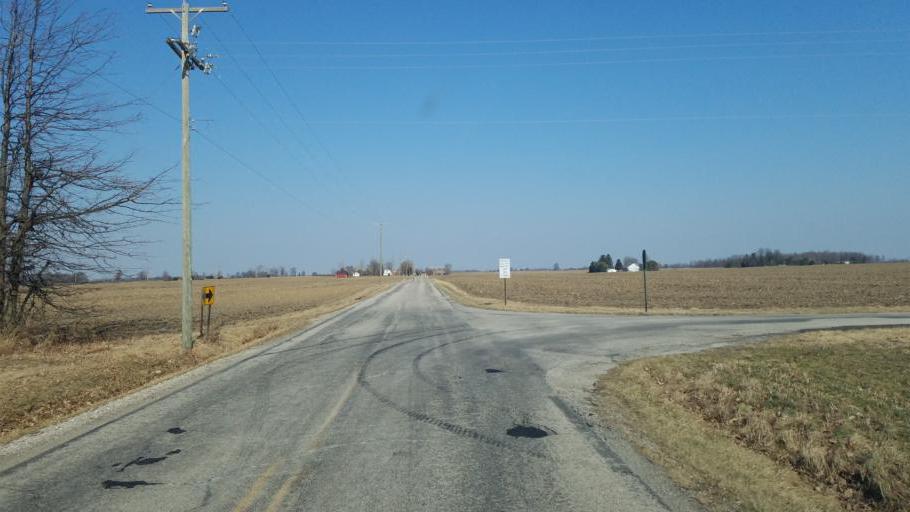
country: US
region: Ohio
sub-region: Crawford County
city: Crestline
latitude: 40.8283
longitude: -82.6965
